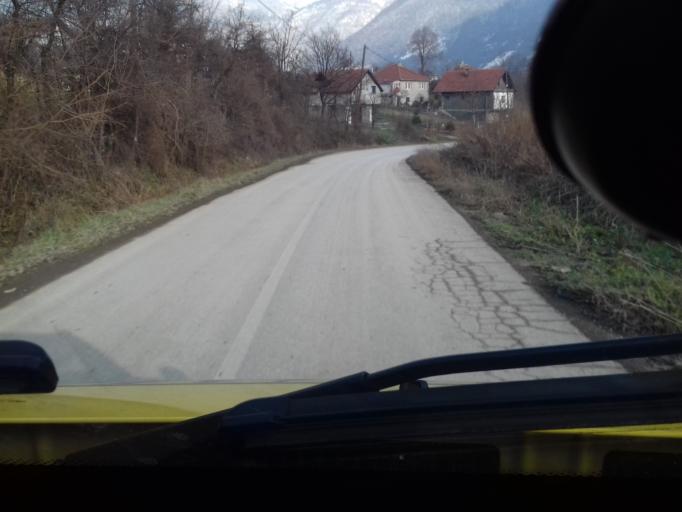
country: BA
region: Federation of Bosnia and Herzegovina
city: Zenica
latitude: 44.2422
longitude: 17.8948
